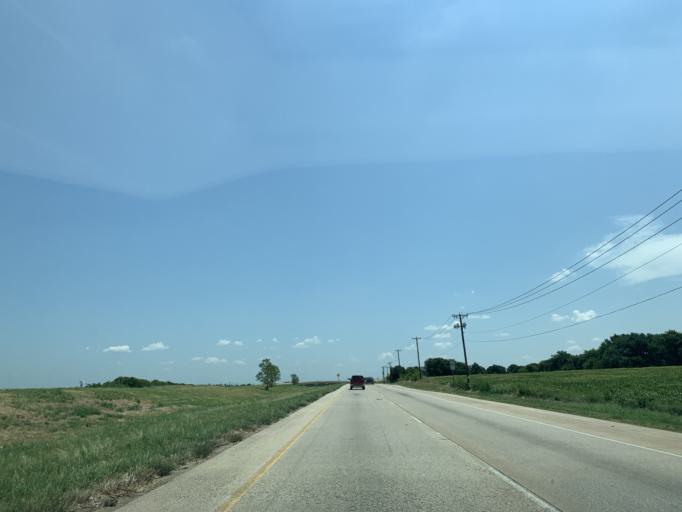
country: US
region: Texas
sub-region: Denton County
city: Roanoke
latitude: 33.0146
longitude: -97.2305
